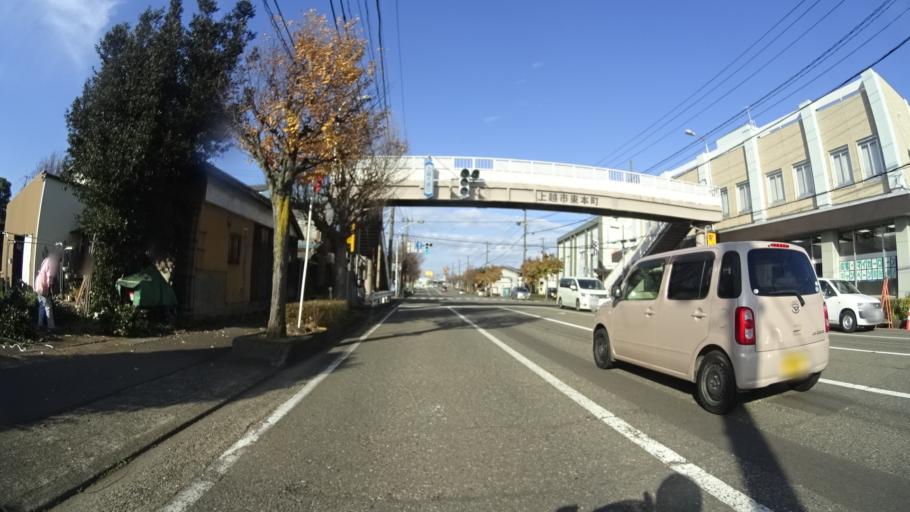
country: JP
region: Niigata
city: Joetsu
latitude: 37.1195
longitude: 138.2519
